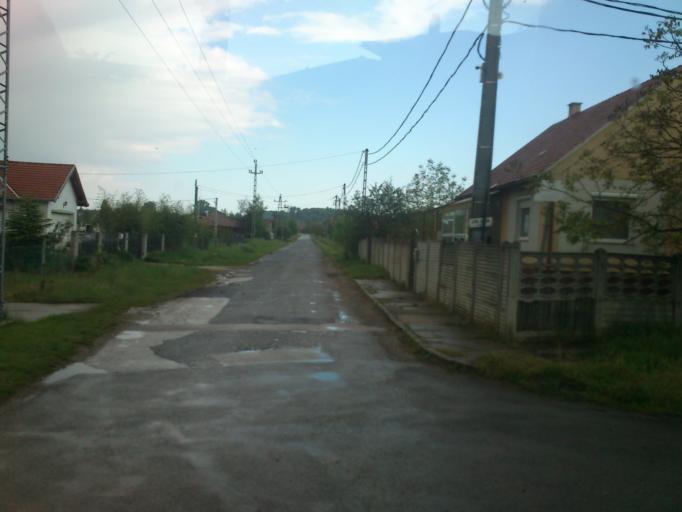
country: HU
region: Komarom-Esztergom
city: Kesztolc
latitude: 47.7085
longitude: 18.7857
